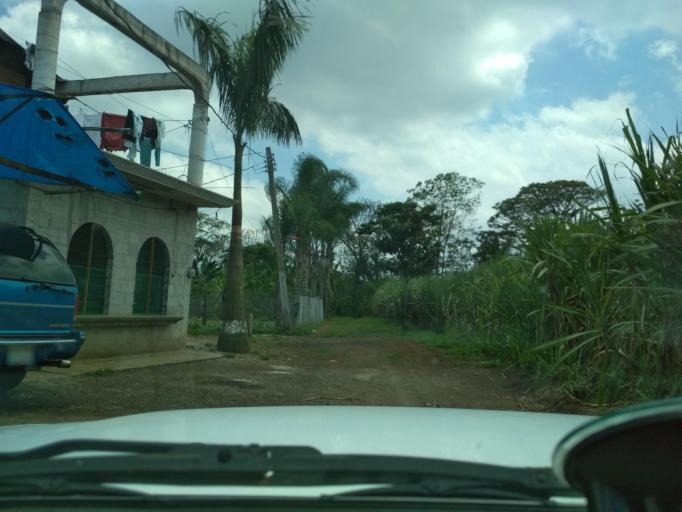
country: MX
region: Veracruz
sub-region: Fortin
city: Monte Salas
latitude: 18.9409
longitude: -97.0147
